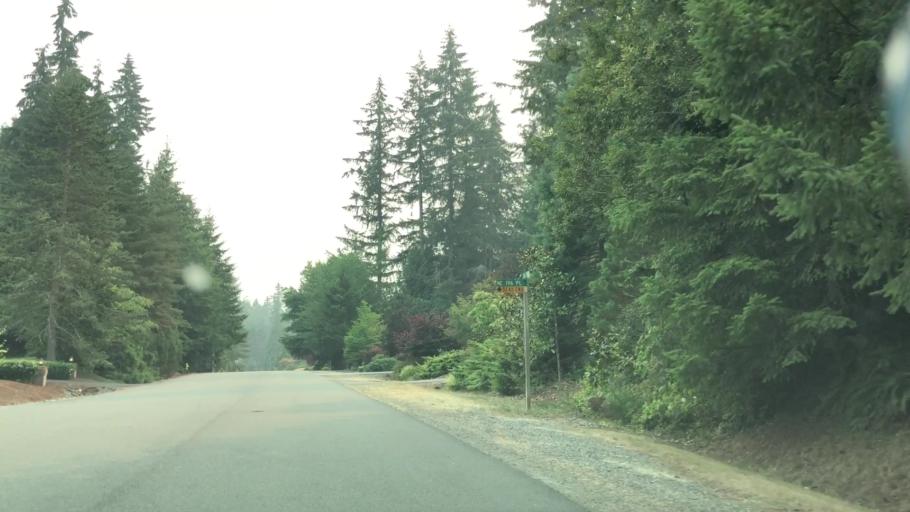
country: US
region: Washington
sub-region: King County
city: Cottage Lake
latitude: 47.7702
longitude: -122.0915
